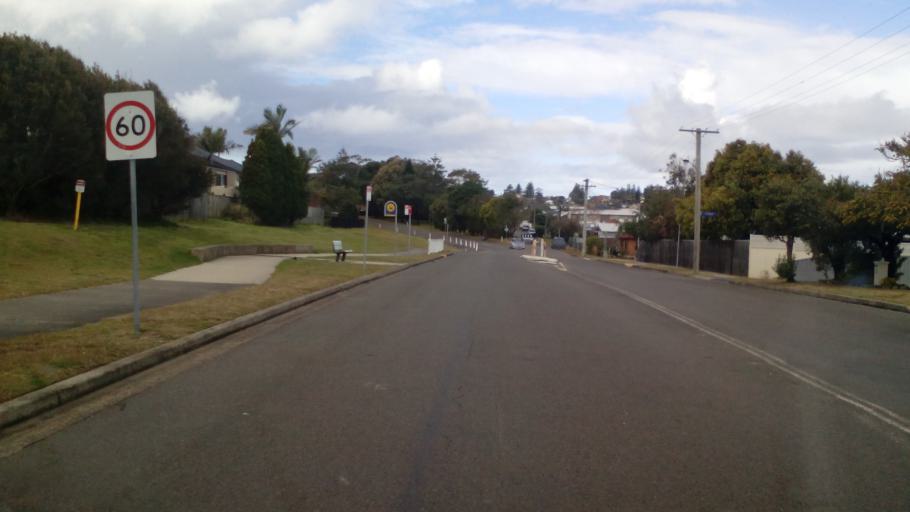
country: AU
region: New South Wales
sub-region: Lake Macquarie Shire
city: Redhead
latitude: -33.0087
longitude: 151.7120
